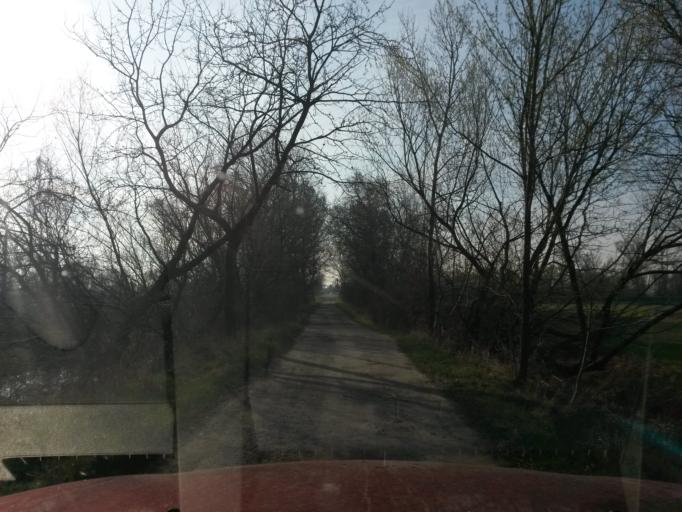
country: SK
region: Nitriansky
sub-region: Okres Komarno
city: Hurbanovo
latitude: 47.8806
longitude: 18.1759
